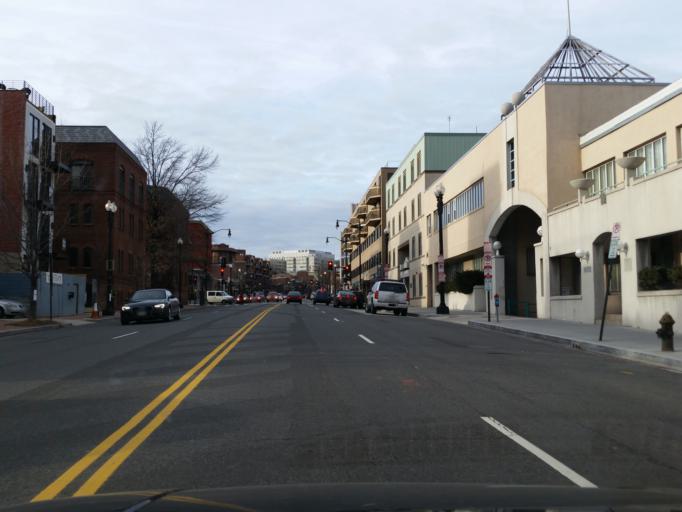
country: US
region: Washington, D.C.
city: Washington, D.C.
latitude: 38.9185
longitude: -77.0700
